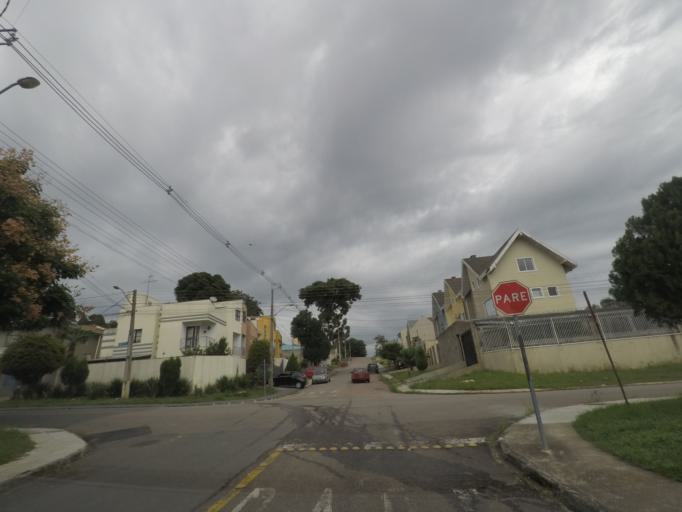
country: BR
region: Parana
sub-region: Pinhais
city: Pinhais
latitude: -25.4662
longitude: -49.2305
